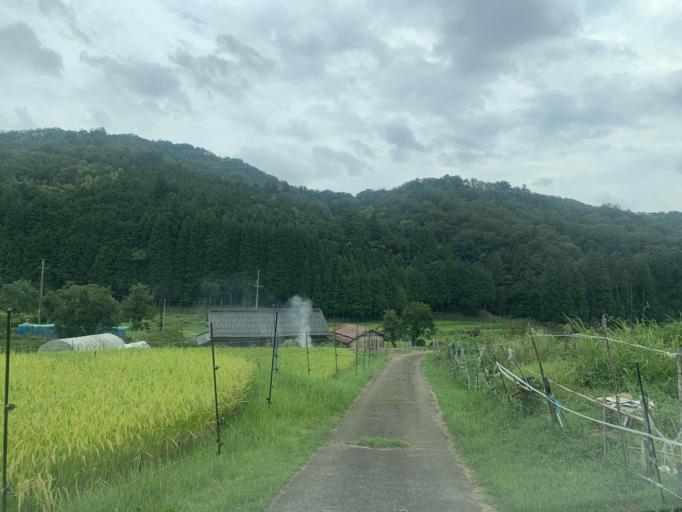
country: JP
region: Kyoto
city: Miyazu
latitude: 35.4465
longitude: 135.1617
